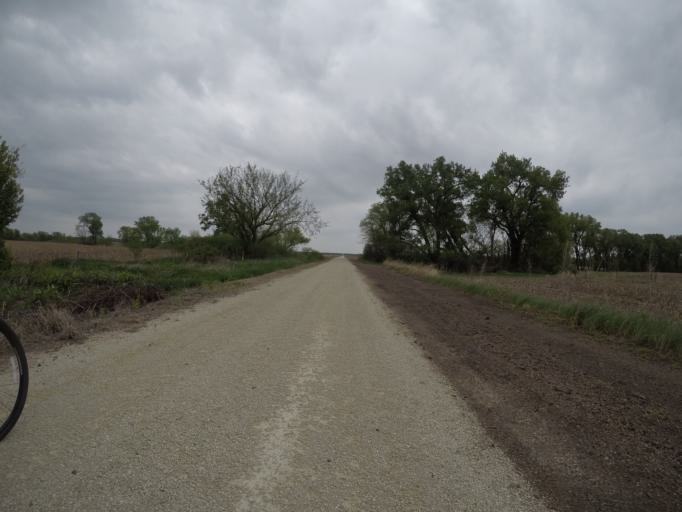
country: US
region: Nebraska
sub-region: Gage County
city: Wymore
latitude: 40.0960
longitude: -96.6021
